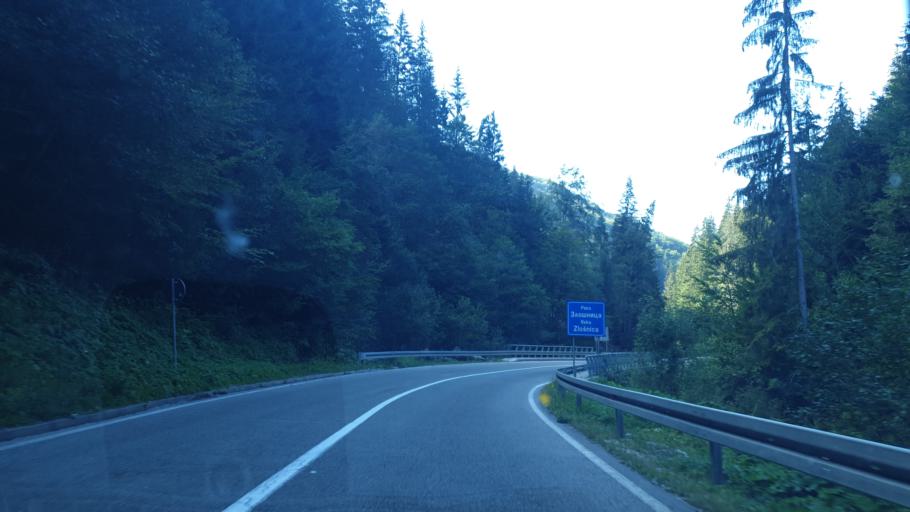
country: RS
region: Central Serbia
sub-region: Zlatiborski Okrug
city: Nova Varos
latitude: 43.4794
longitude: 19.8307
